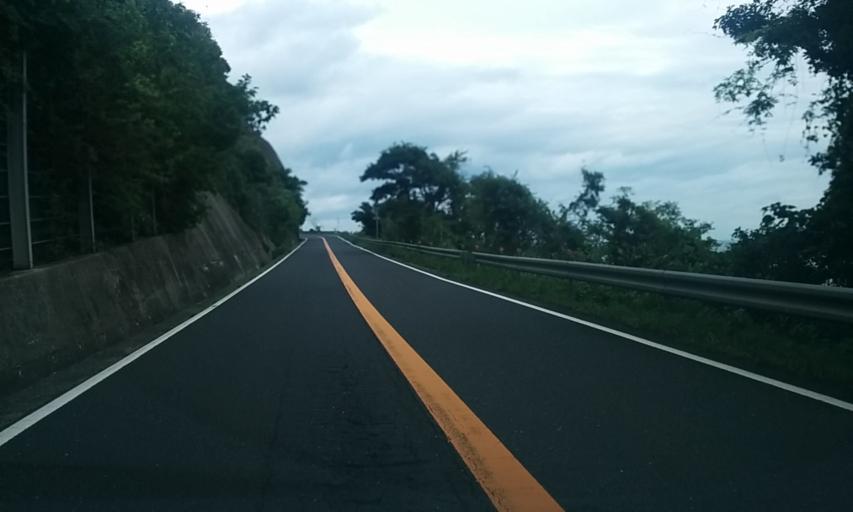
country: JP
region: Kyoto
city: Miyazu
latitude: 35.5257
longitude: 135.2716
